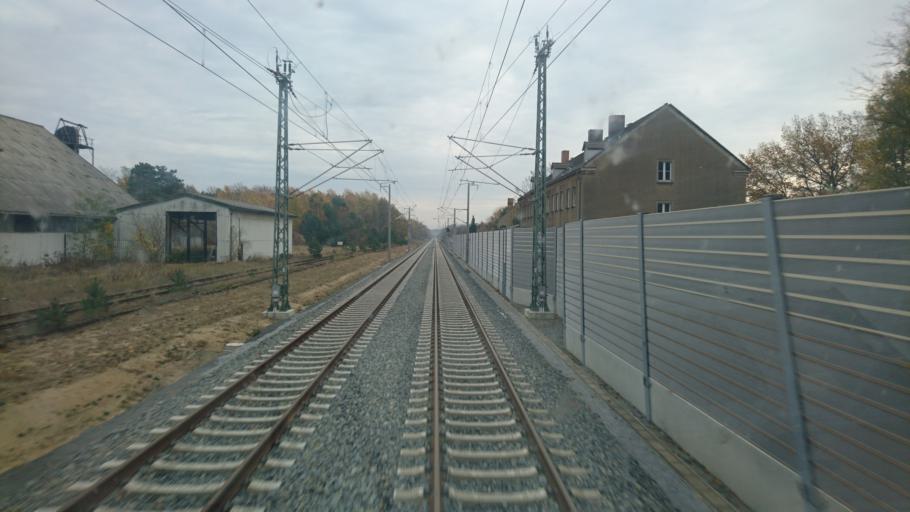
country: DE
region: Saxony
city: Mucka
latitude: 51.3196
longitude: 14.7070
